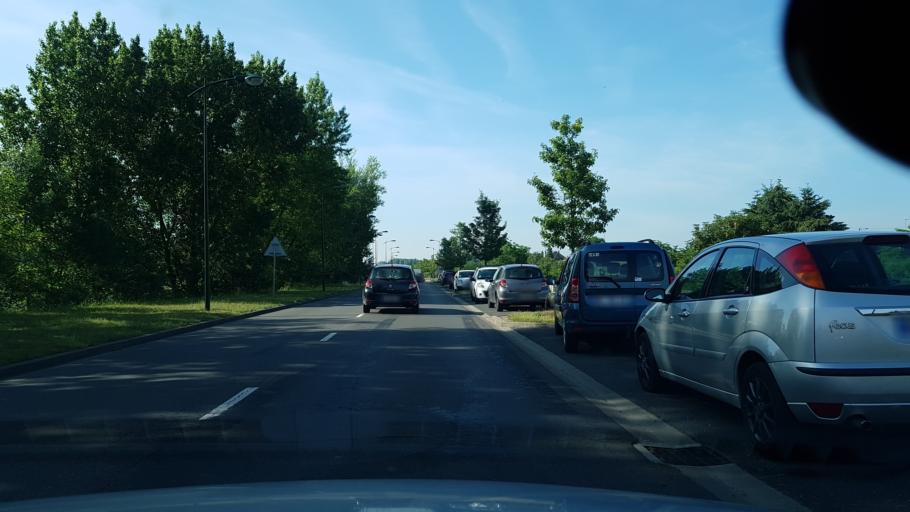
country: FR
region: Centre
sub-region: Departement du Loir-et-Cher
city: Selles-sur-Cher
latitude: 47.2776
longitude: 1.5580
